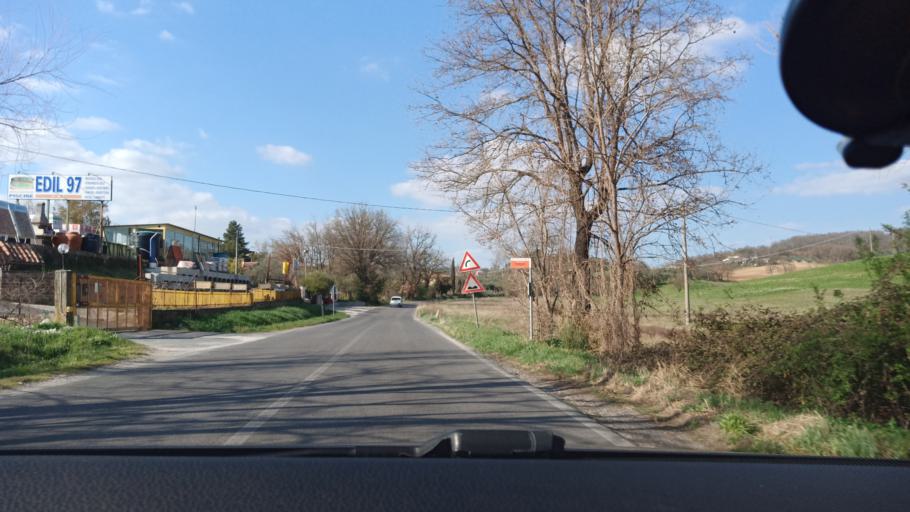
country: IT
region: Latium
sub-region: Citta metropolitana di Roma Capitale
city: Torrita Tiberina
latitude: 42.2589
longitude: 12.6391
